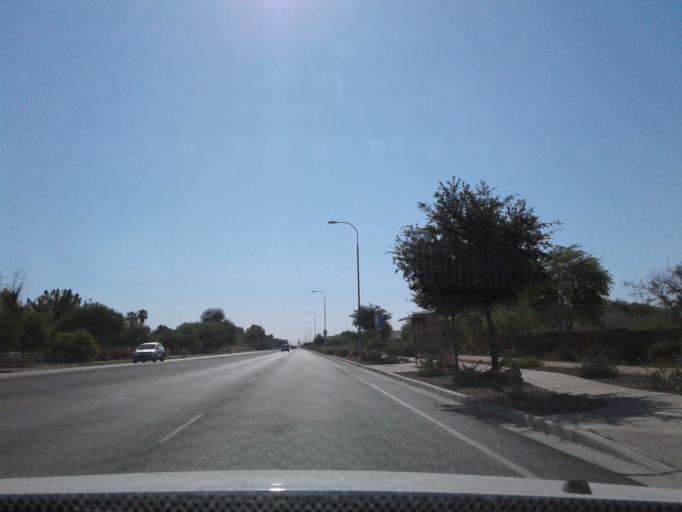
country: US
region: Arizona
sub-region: Maricopa County
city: Laveen
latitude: 33.3773
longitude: -112.2109
